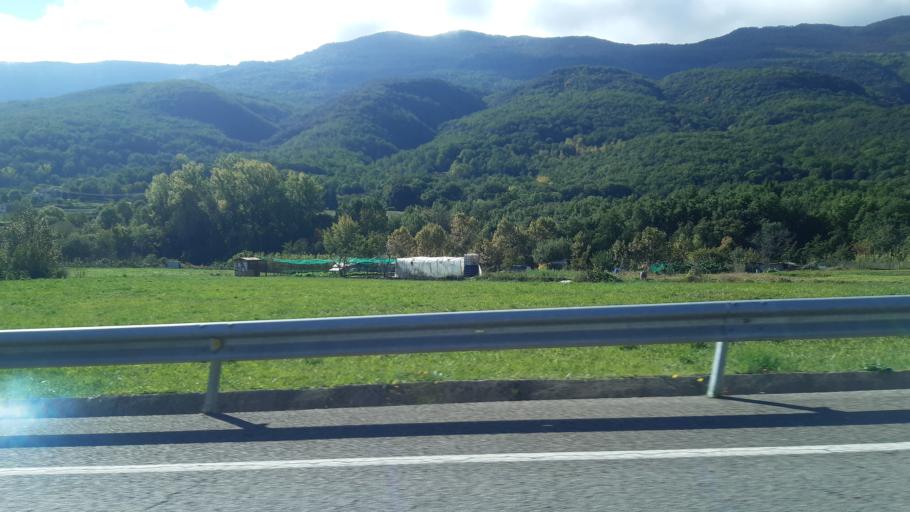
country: ES
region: Catalonia
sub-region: Provincia de Girona
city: les Planes d'Hostoles
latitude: 42.0615
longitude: 2.5346
